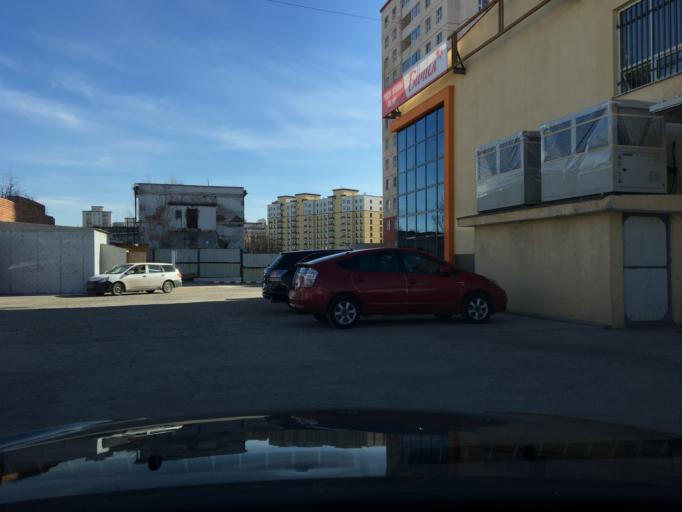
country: MN
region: Ulaanbaatar
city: Ulaanbaatar
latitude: 47.8927
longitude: 106.8943
